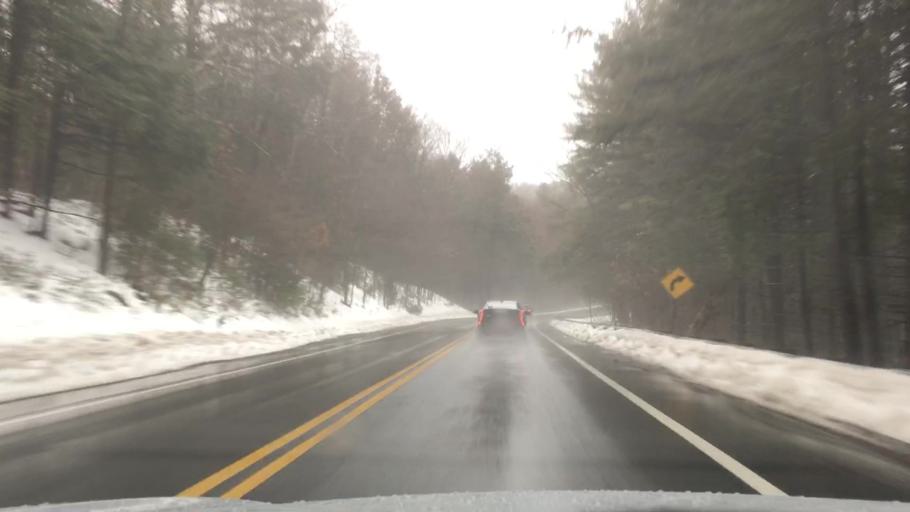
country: US
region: Massachusetts
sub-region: Franklin County
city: Shutesbury
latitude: 42.4274
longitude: -72.3983
